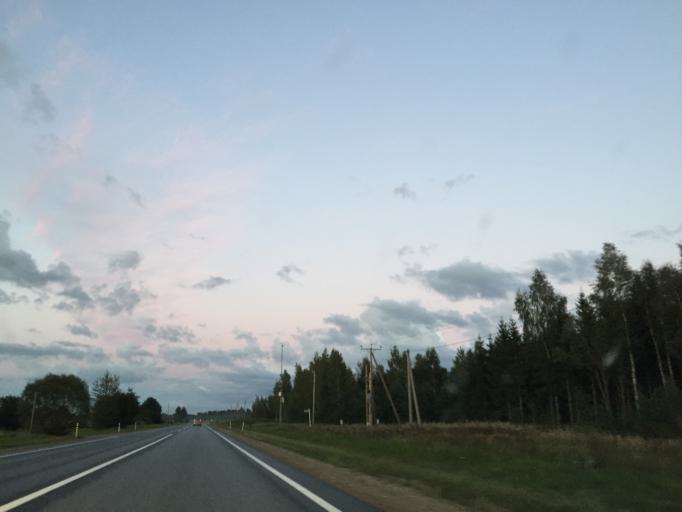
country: LV
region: Jurmala
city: Jurmala
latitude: 56.8944
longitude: 23.7106
